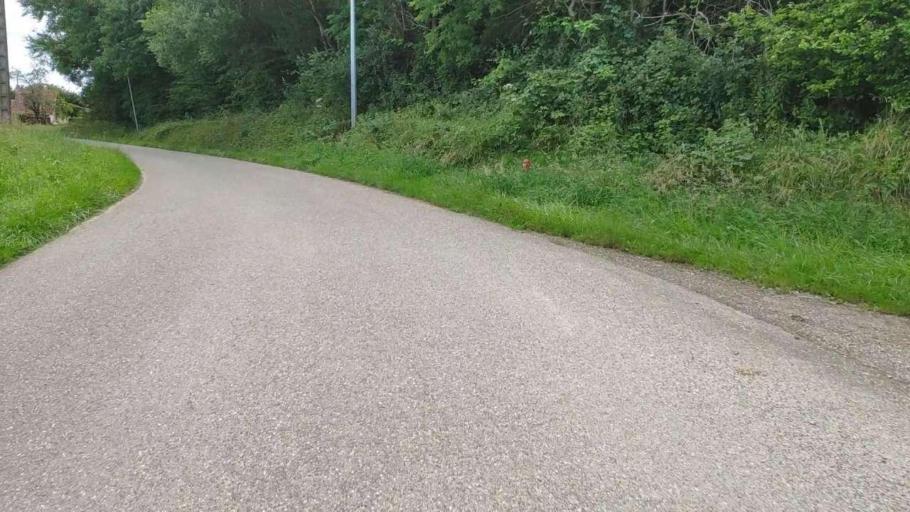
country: FR
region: Franche-Comte
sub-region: Departement du Jura
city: Chaussin
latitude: 46.8878
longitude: 5.4450
